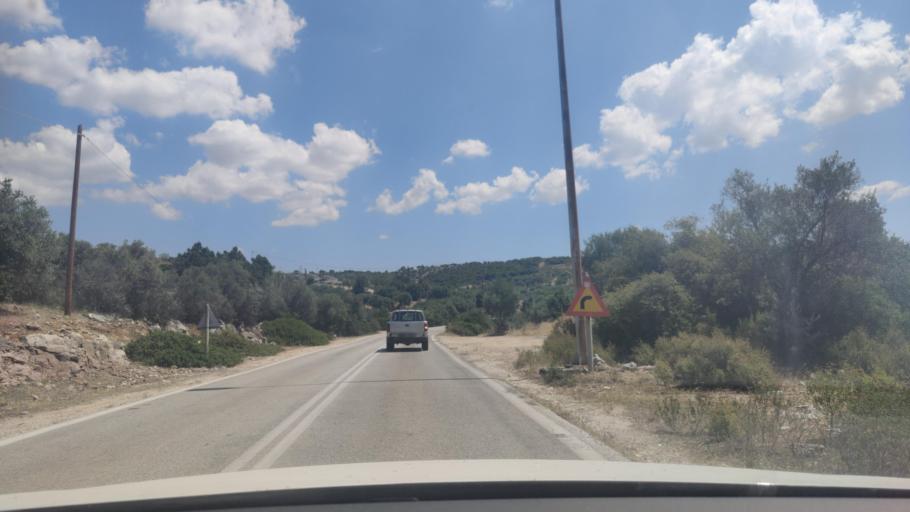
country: GR
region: East Macedonia and Thrace
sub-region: Nomos Kavalas
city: Limenaria
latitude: 40.6394
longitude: 24.5244
